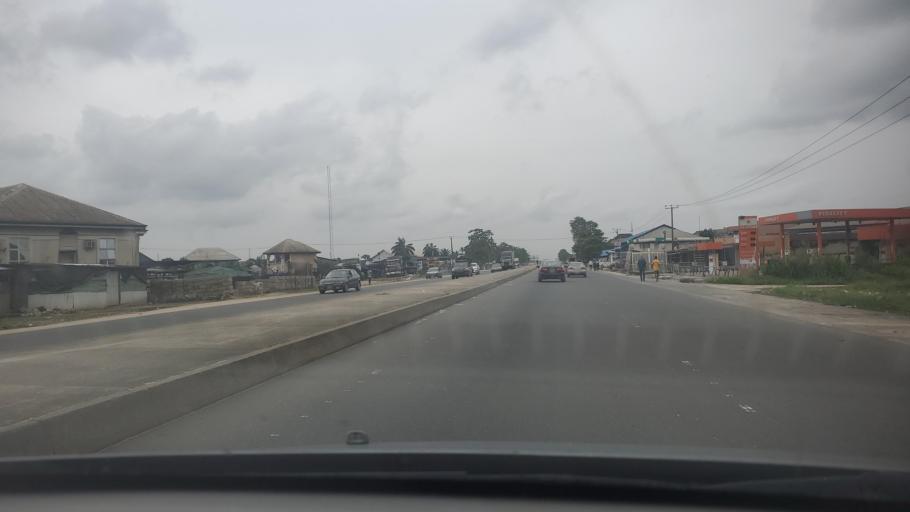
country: NG
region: Rivers
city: Port Harcourt
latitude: 4.8708
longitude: 6.9680
